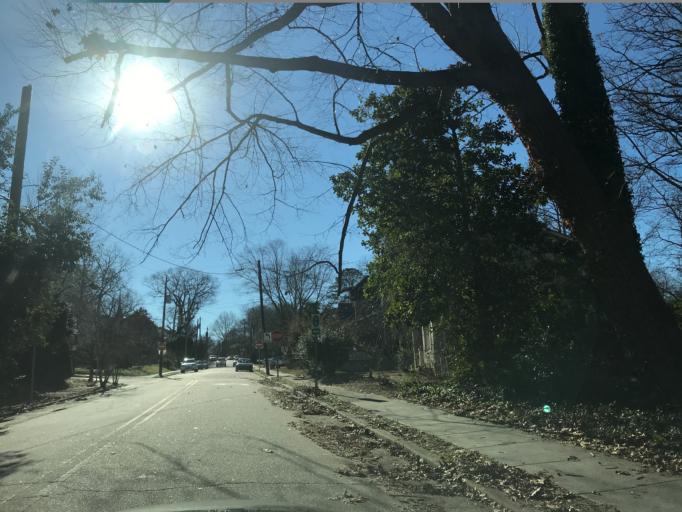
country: US
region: North Carolina
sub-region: Wake County
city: West Raleigh
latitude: 35.8073
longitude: -78.6439
